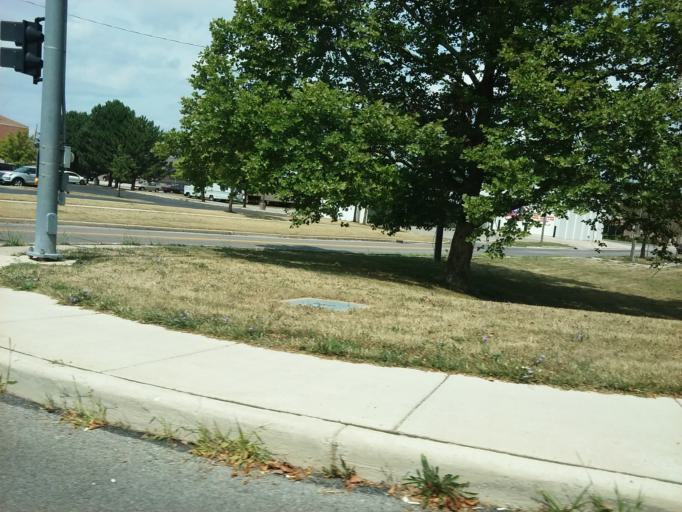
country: US
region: Ohio
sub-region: Hancock County
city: Findlay
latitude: 41.0394
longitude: -83.6466
